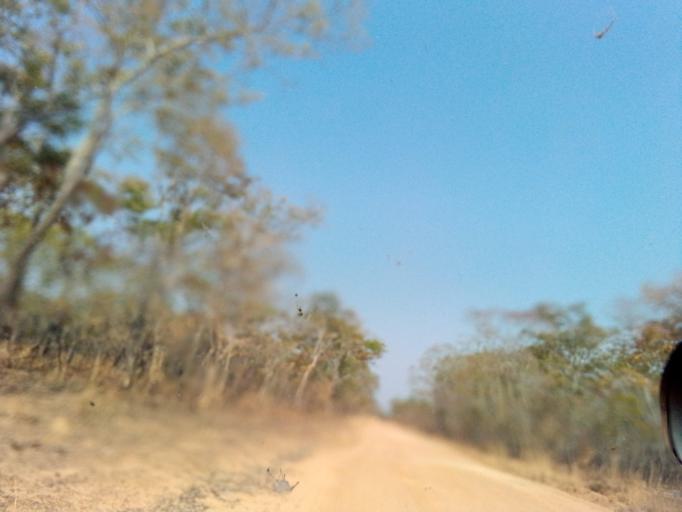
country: ZM
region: Northern
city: Mpika
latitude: -12.2418
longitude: 30.8286
